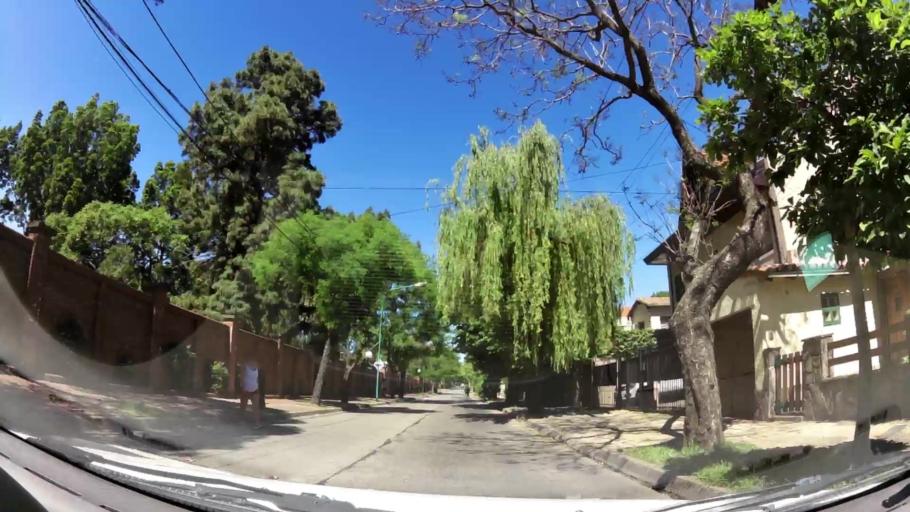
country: AR
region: Buenos Aires
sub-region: Partido de Vicente Lopez
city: Olivos
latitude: -34.5143
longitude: -58.4848
